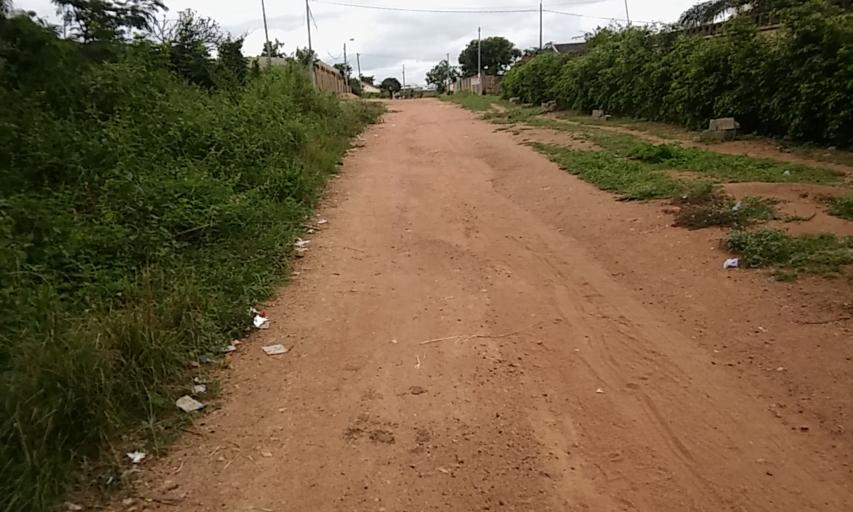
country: CI
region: Vallee du Bandama
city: Bouake
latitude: 7.6932
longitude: -5.0603
